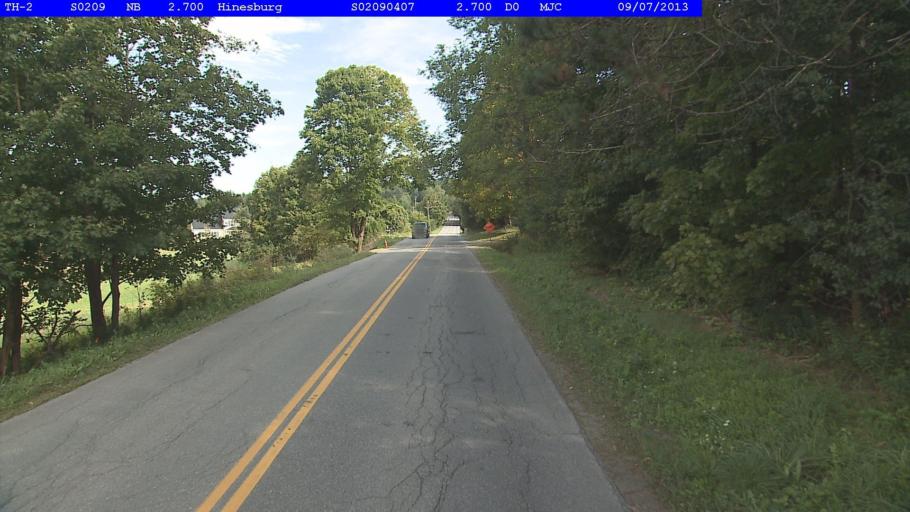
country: US
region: Vermont
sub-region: Chittenden County
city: Hinesburg
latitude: 44.3501
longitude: -73.0765
